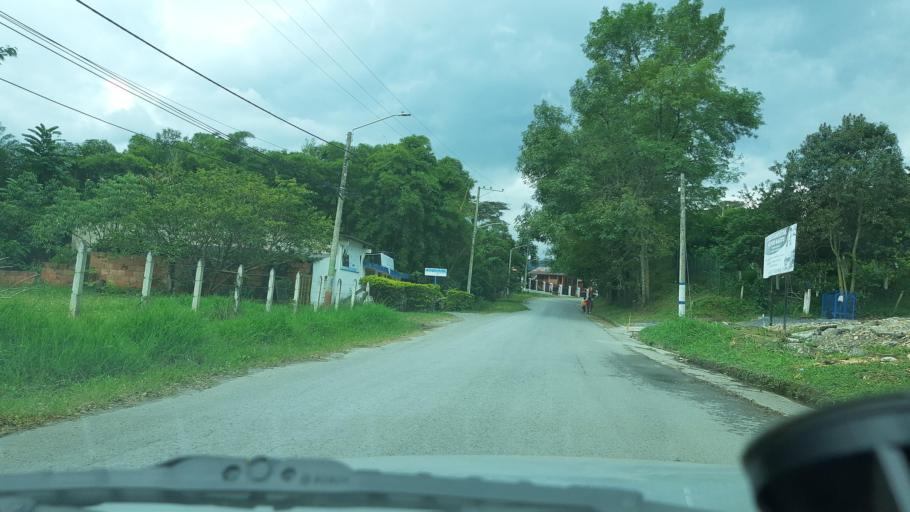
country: CO
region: Boyaca
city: Moniquira
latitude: 5.8856
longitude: -73.5775
